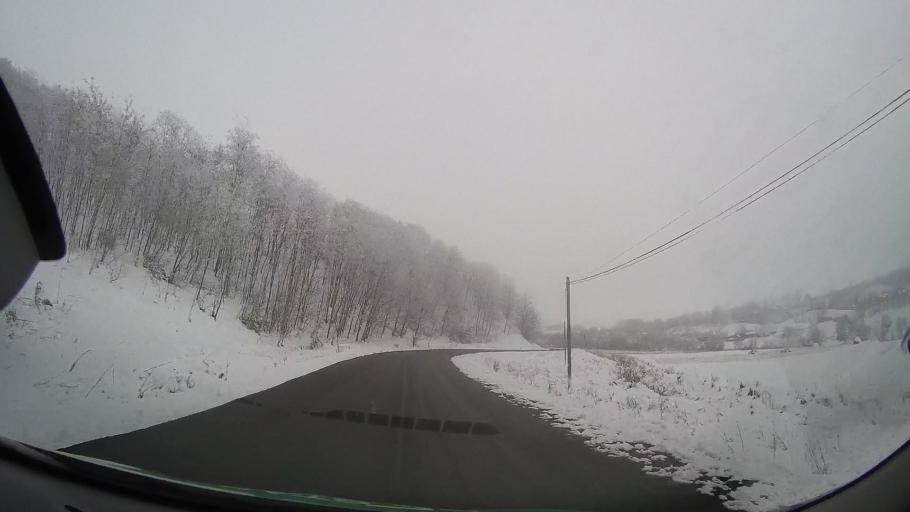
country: RO
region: Bacau
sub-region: Comuna Oncesti
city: Oncesti
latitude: 46.4760
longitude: 27.2571
